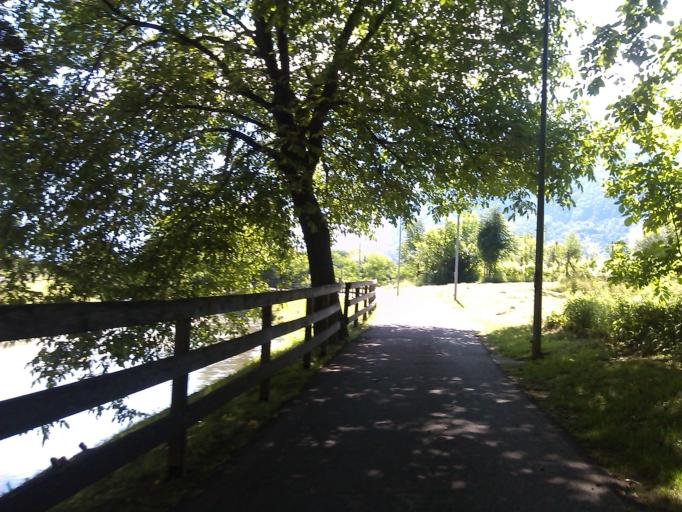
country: IT
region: Trentino-Alto Adige
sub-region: Provincia di Trento
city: Borgo
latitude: 46.0539
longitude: 11.4670
